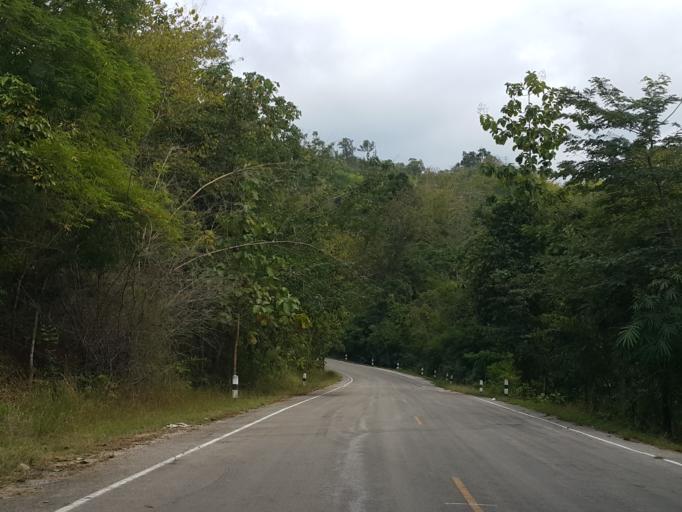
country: TH
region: Lampang
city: Chae Hom
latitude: 18.6510
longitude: 99.4998
